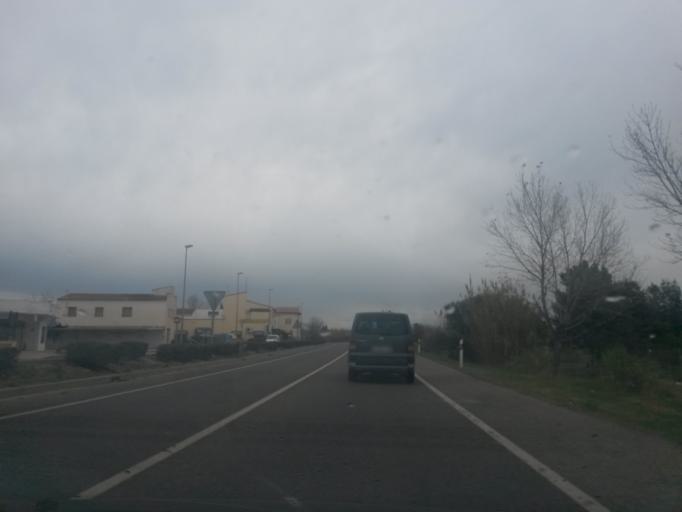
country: ES
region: Catalonia
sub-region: Provincia de Girona
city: Vilamalla
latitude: 42.2396
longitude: 2.9704
